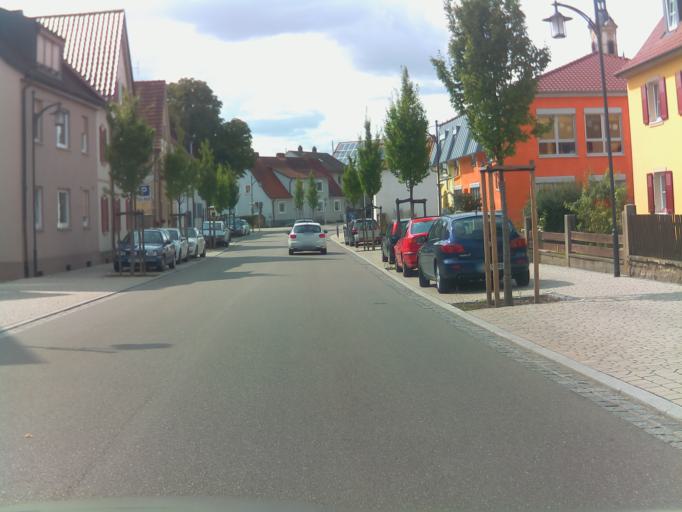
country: DE
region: Bavaria
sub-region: Regierungsbezirk Unterfranken
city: Bergrheinfeld
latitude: 50.0056
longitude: 10.1835
